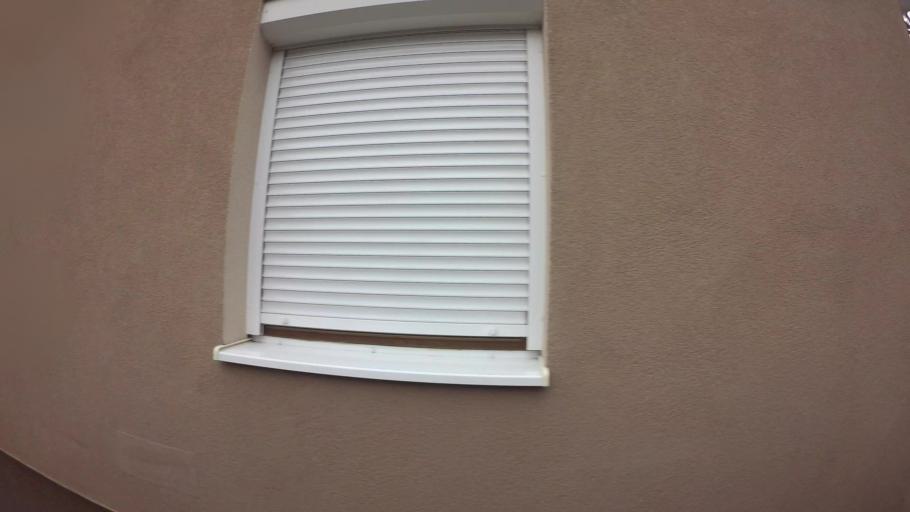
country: BA
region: Federation of Bosnia and Herzegovina
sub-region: Hercegovacko-Bosanski Kanton
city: Mostar
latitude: 43.3313
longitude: 17.7971
